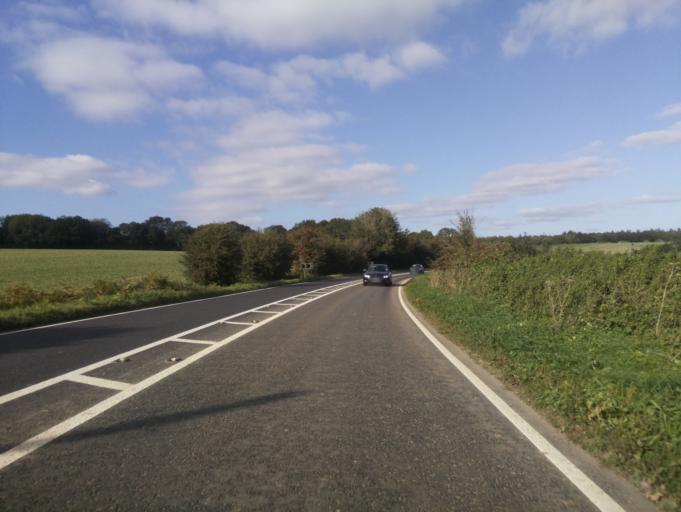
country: GB
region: England
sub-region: Hampshire
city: Four Marks
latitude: 51.1818
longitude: -1.0601
